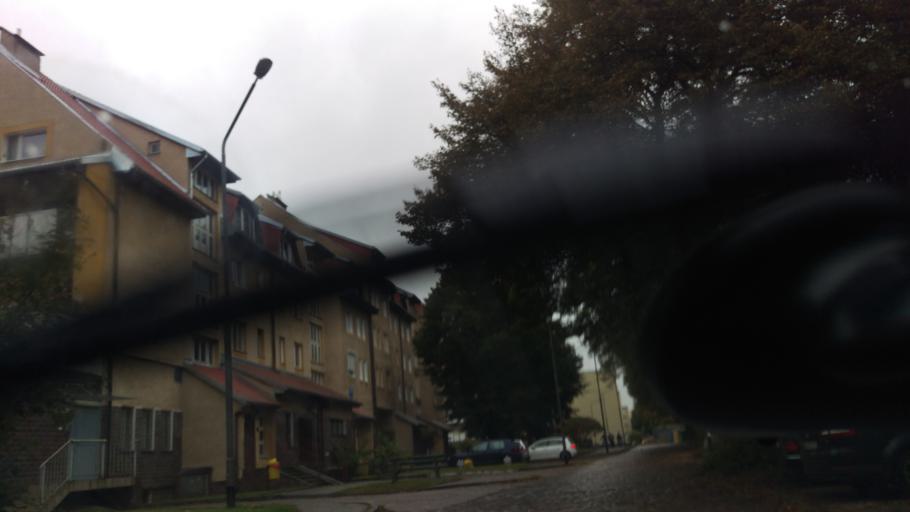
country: PL
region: West Pomeranian Voivodeship
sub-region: Szczecin
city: Szczecin
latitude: 53.3956
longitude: 14.6706
